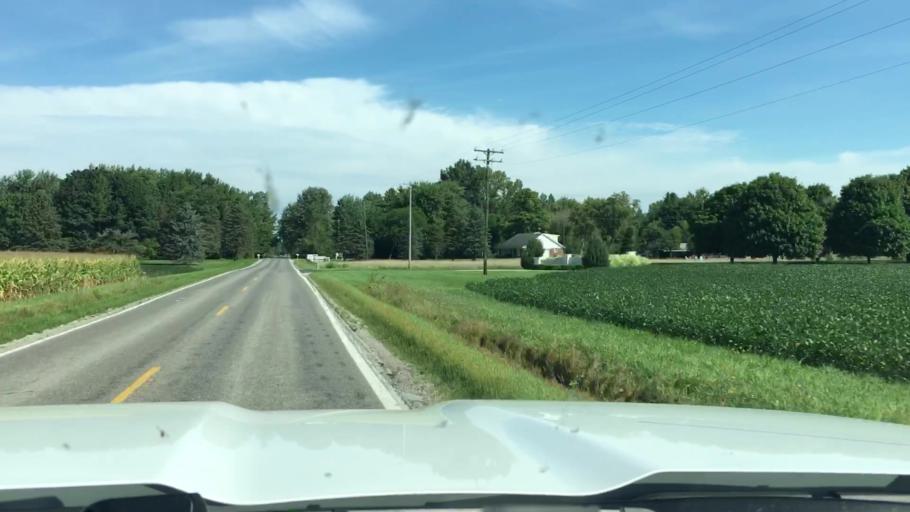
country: US
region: Michigan
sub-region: Saginaw County
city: Hemlock
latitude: 43.4698
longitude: -84.2303
